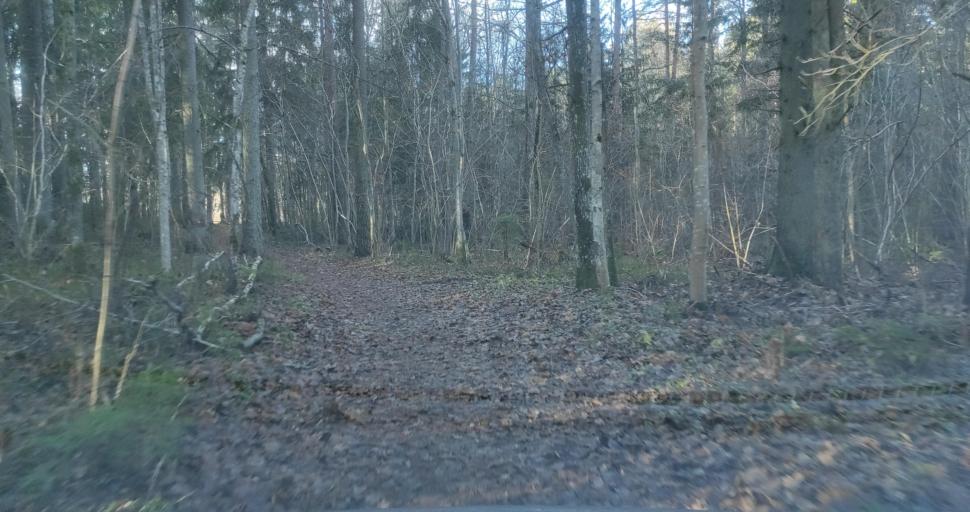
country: LV
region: Kuldigas Rajons
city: Kuldiga
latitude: 56.9611
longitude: 21.9305
